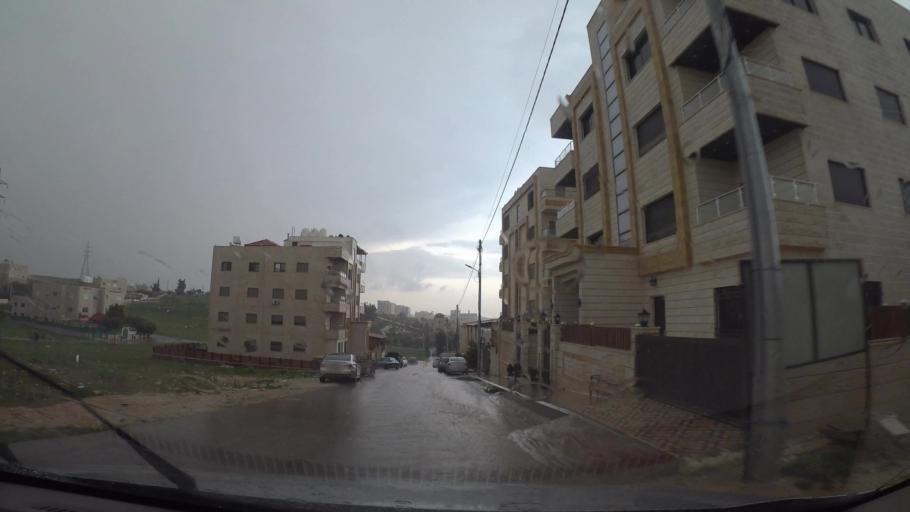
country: JO
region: Amman
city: Umm as Summaq
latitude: 31.8782
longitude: 35.8617
